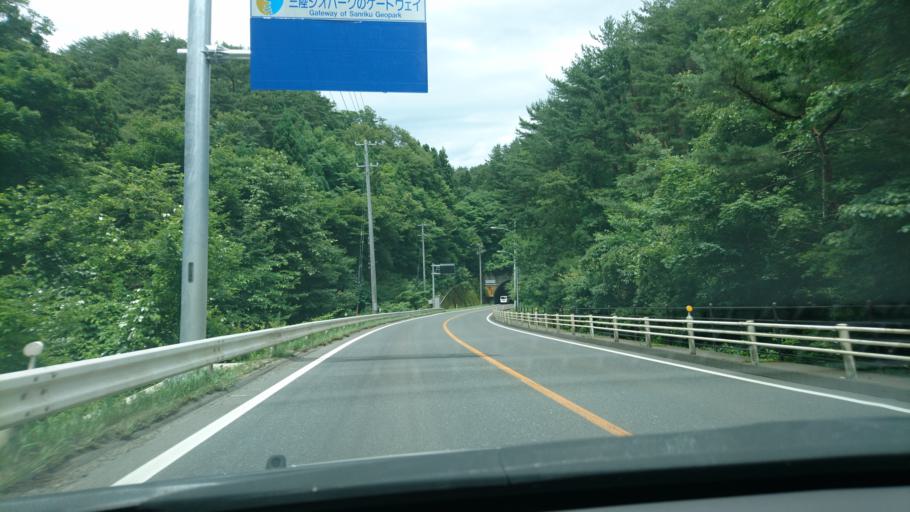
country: JP
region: Iwate
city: Miyako
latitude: 39.7163
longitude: 141.9680
